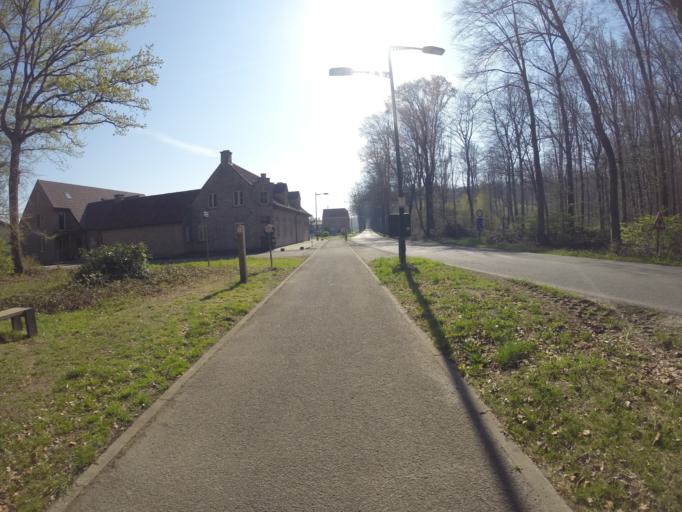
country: BE
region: Flanders
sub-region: Provincie Oost-Vlaanderen
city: Knesselare
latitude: 51.0928
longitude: 3.3897
